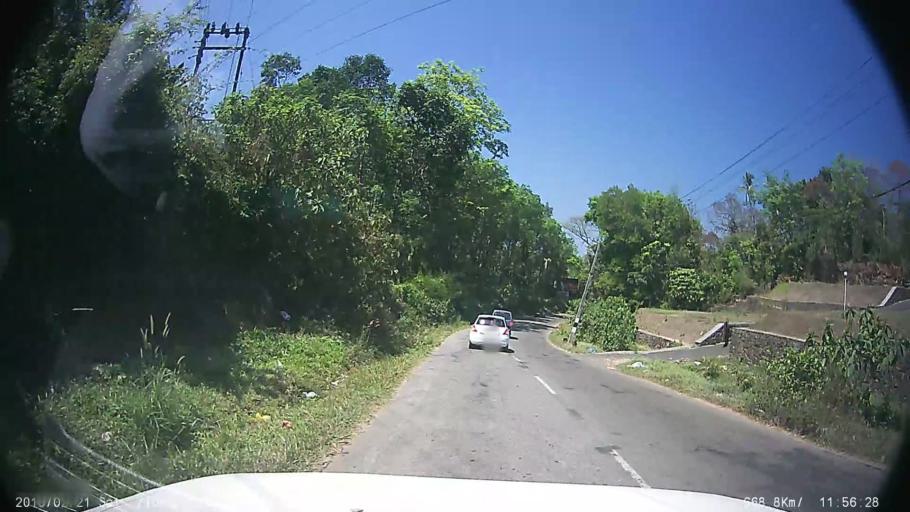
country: IN
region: Kerala
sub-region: Kottayam
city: Lalam
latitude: 9.7412
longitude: 76.6927
